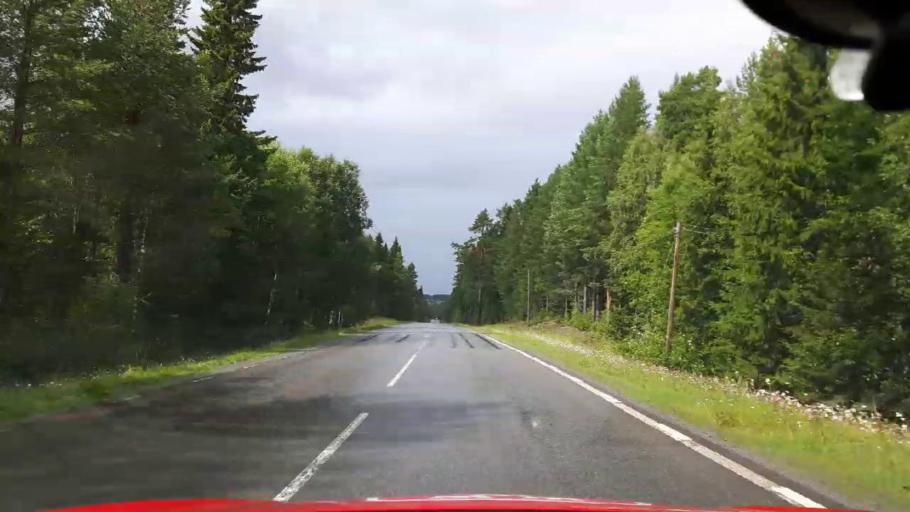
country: SE
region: Jaemtland
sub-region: Krokoms Kommun
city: Krokom
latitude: 63.3387
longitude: 14.2740
